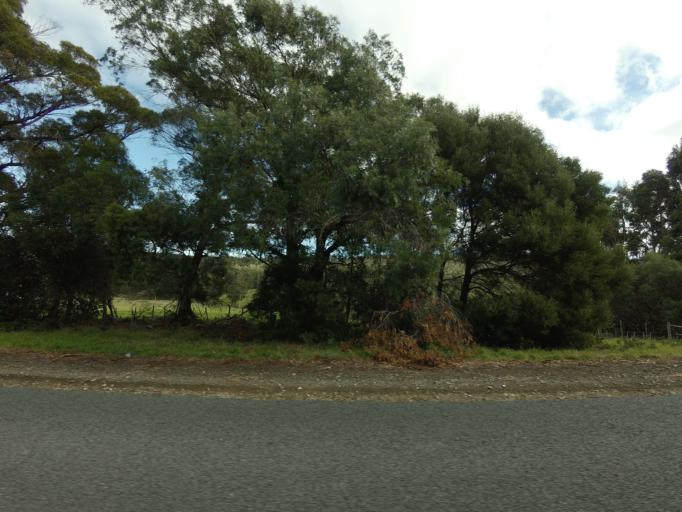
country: AU
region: Tasmania
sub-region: Clarence
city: Sandford
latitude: -43.0833
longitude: 147.7377
